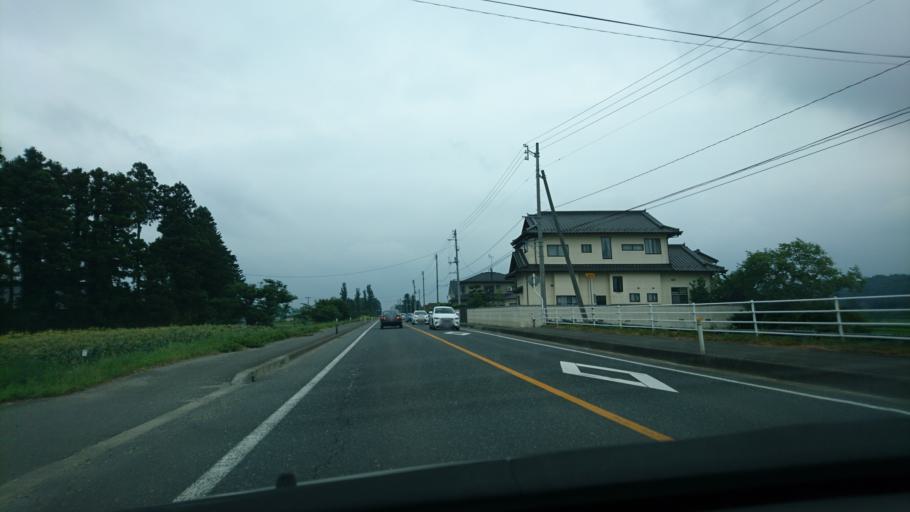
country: JP
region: Miyagi
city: Furukawa
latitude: 38.6917
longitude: 140.8477
